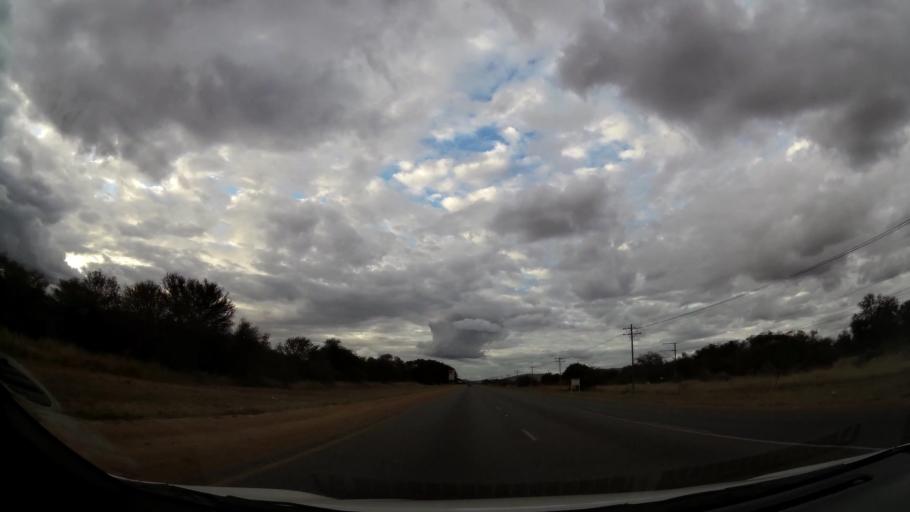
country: ZA
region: Limpopo
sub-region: Waterberg District Municipality
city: Mokopane
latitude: -24.2359
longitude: 28.9969
